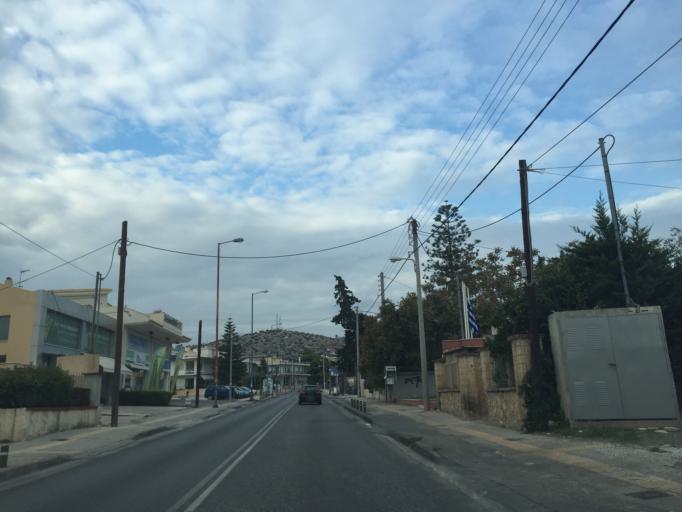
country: GR
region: Attica
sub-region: Nomarchia Anatolikis Attikis
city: Vari
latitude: 37.8281
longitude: 23.8036
